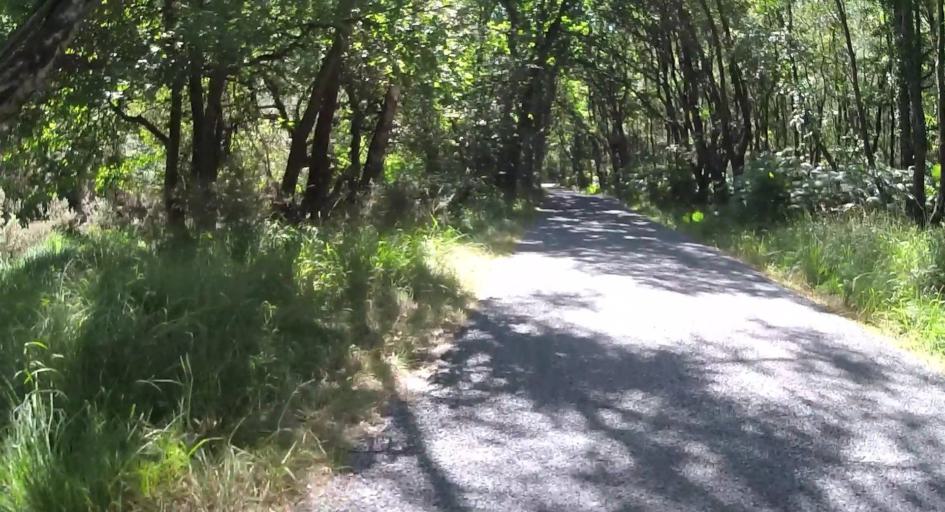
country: GB
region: England
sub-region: Dorset
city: Wareham
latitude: 50.6770
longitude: -2.0627
